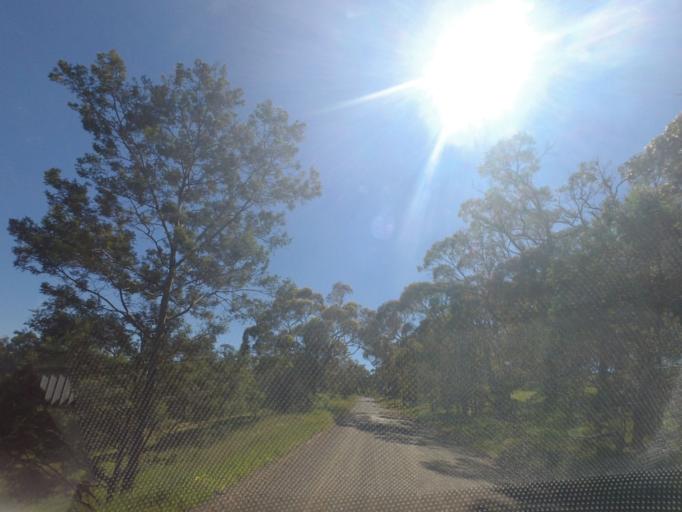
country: AU
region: Victoria
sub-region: Whittlesea
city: Whittlesea
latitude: -37.3854
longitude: 144.9617
